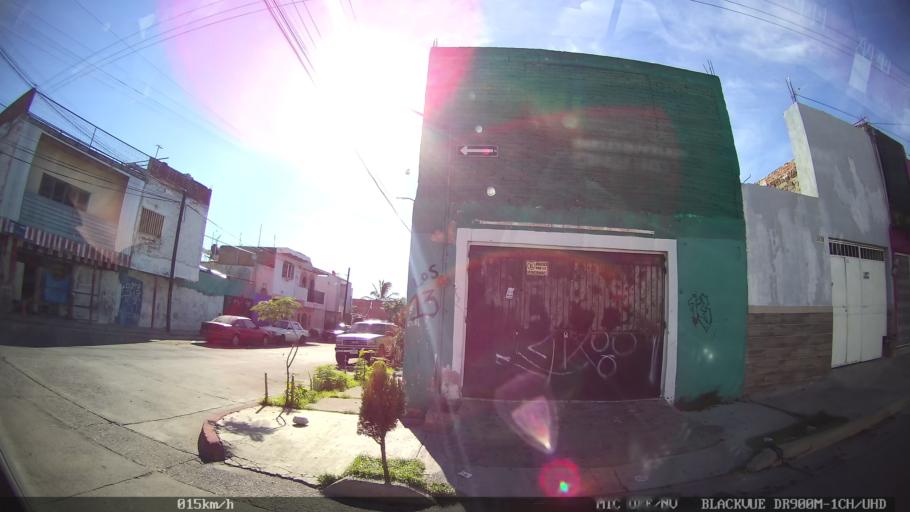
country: MX
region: Jalisco
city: Tlaquepaque
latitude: 20.6973
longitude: -103.2789
